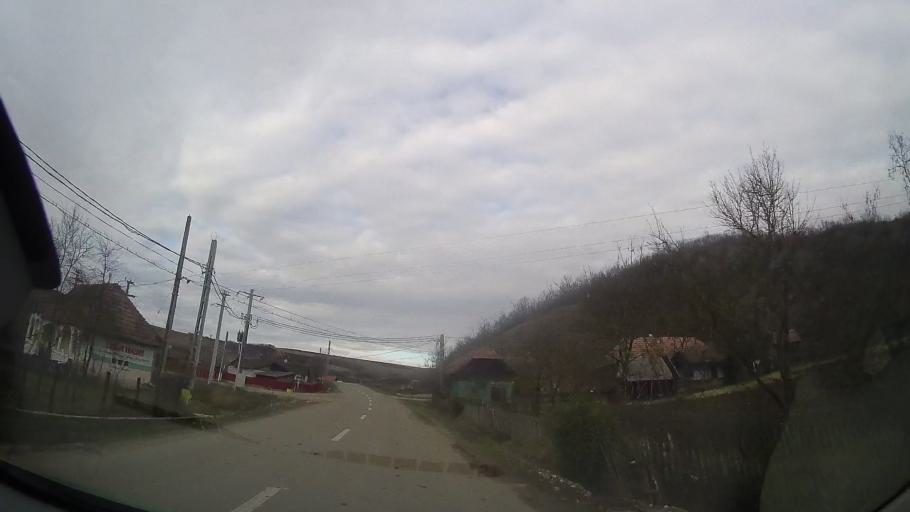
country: RO
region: Bistrita-Nasaud
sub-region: Comuna Silvasu de Campie
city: Silvasu de Campie
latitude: 46.7843
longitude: 24.2878
